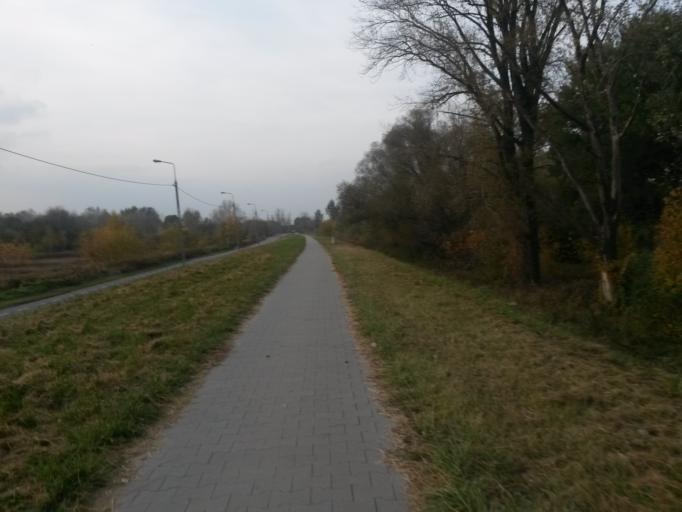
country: PL
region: Masovian Voivodeship
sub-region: Warszawa
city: Wilanow
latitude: 52.1876
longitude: 21.1062
